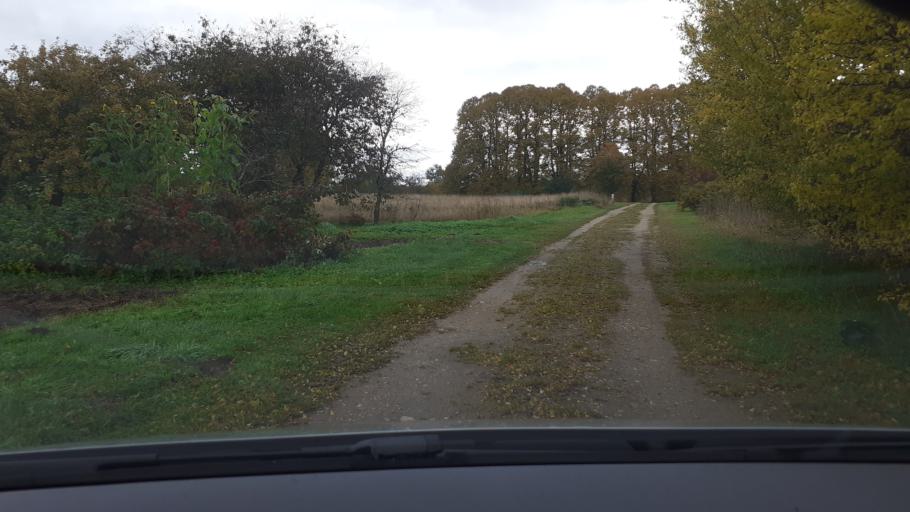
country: LV
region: Kuldigas Rajons
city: Kuldiga
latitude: 57.0169
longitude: 21.9047
